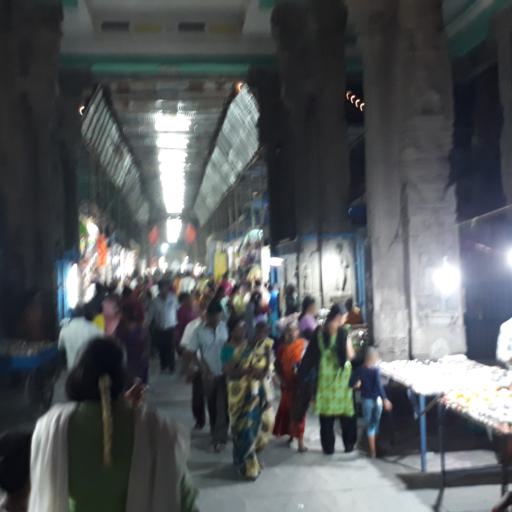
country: IN
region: Tamil Nadu
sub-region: Kancheepuram
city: Kanchipuram
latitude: 12.8448
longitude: 79.7000
